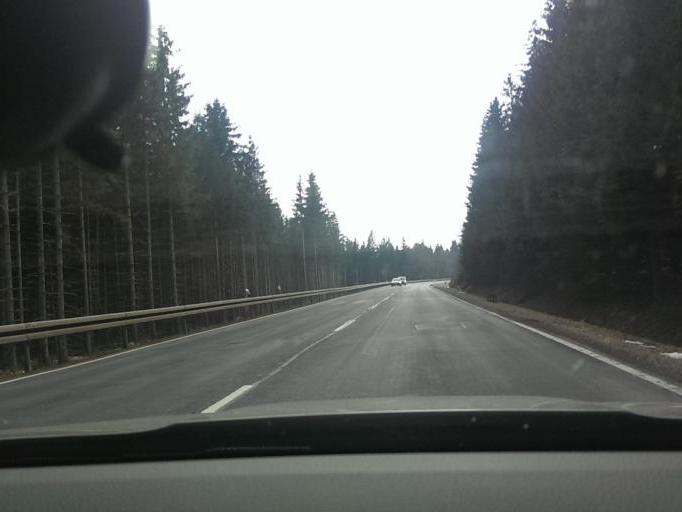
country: DE
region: Thuringia
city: Oberhof
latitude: 50.7275
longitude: 10.7266
